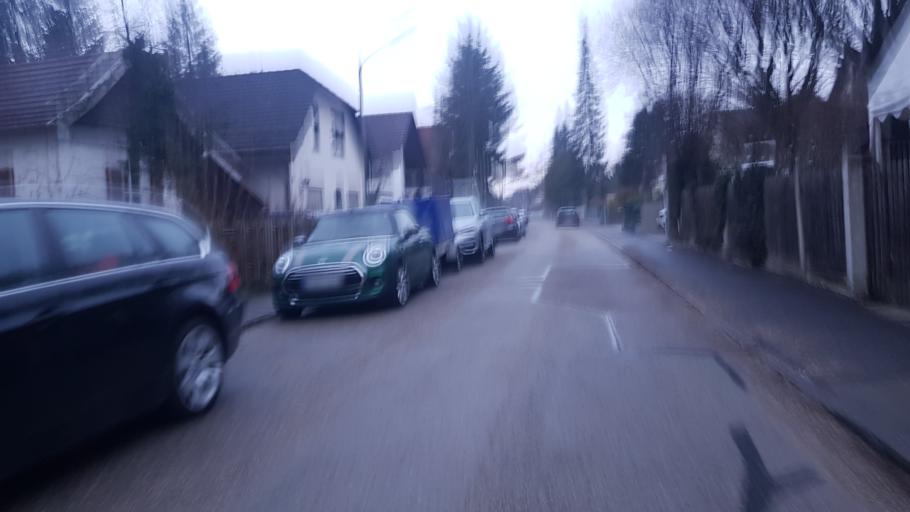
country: DE
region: Bavaria
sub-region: Upper Bavaria
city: Pasing
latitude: 48.1624
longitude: 11.4528
